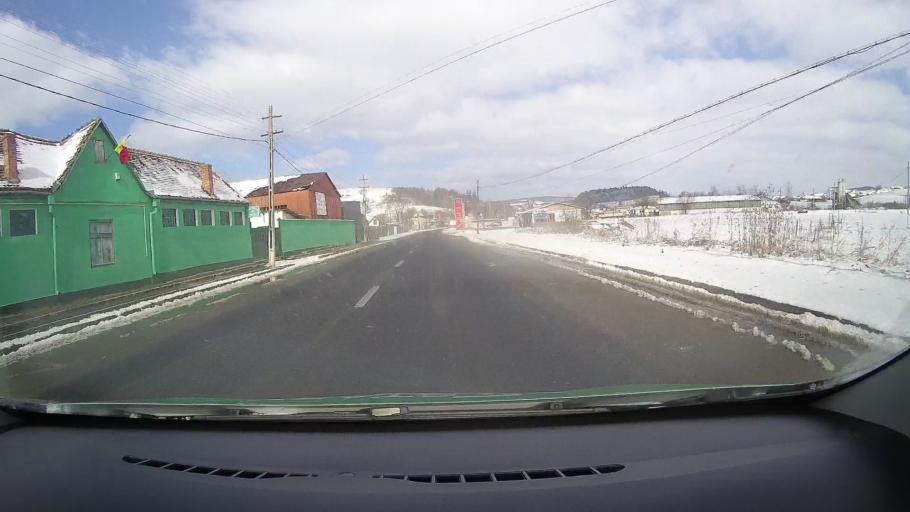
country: RO
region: Sibiu
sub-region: Oras Agnita
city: Agnita
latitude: 45.9693
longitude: 24.6049
